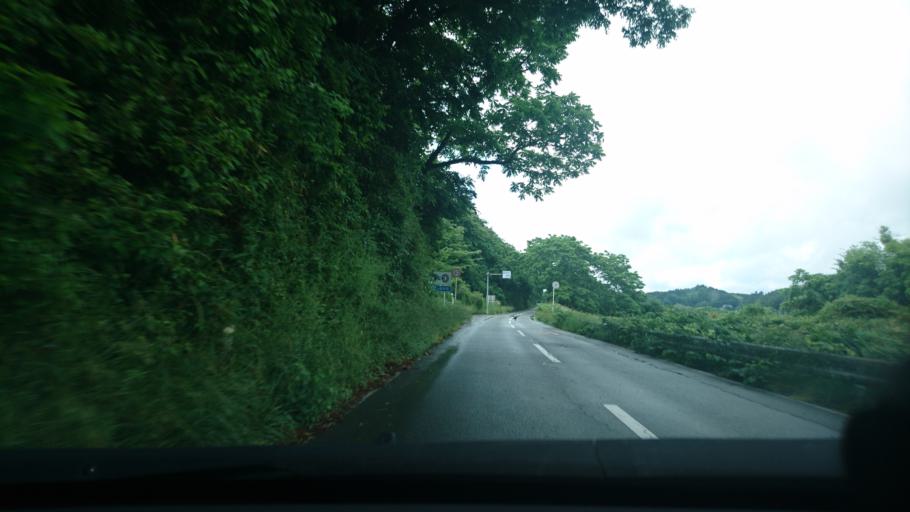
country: JP
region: Miyagi
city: Wakuya
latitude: 38.6751
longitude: 141.2833
